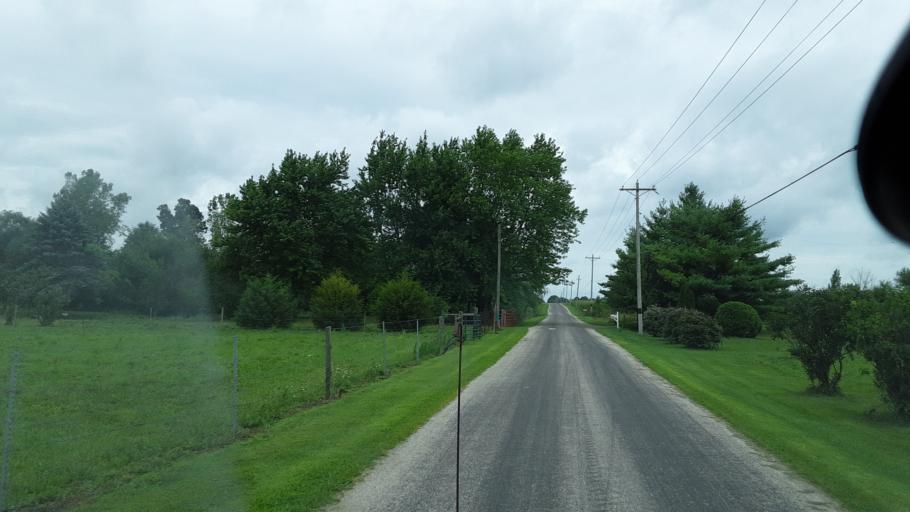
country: US
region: Indiana
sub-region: Adams County
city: Geneva
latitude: 40.5242
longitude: -85.0101
